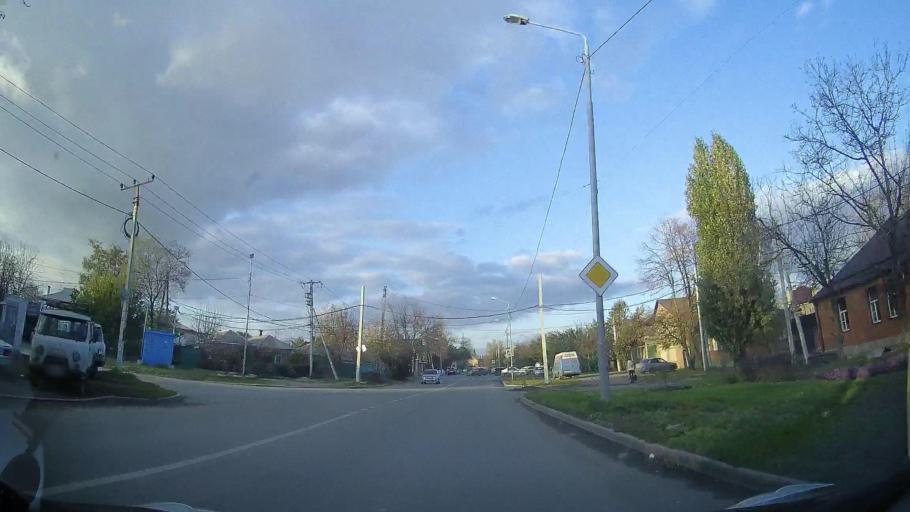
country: RU
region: Rostov
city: Imeni Chkalova
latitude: 47.2438
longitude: 39.7777
